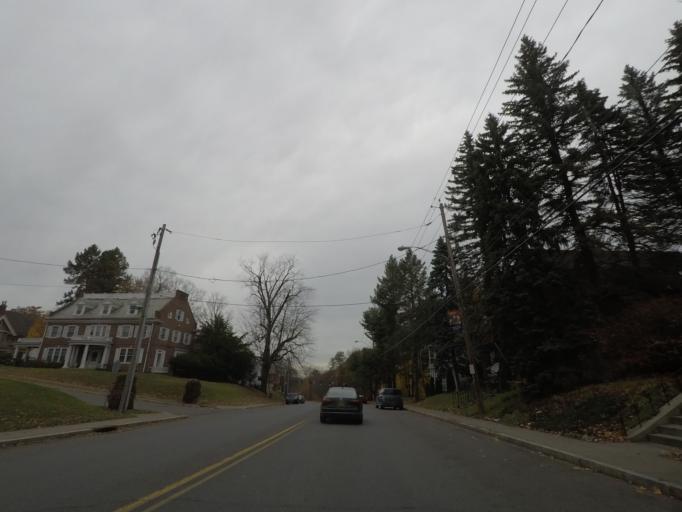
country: US
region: New York
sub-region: Rensselaer County
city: Troy
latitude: 42.7175
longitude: -73.6709
